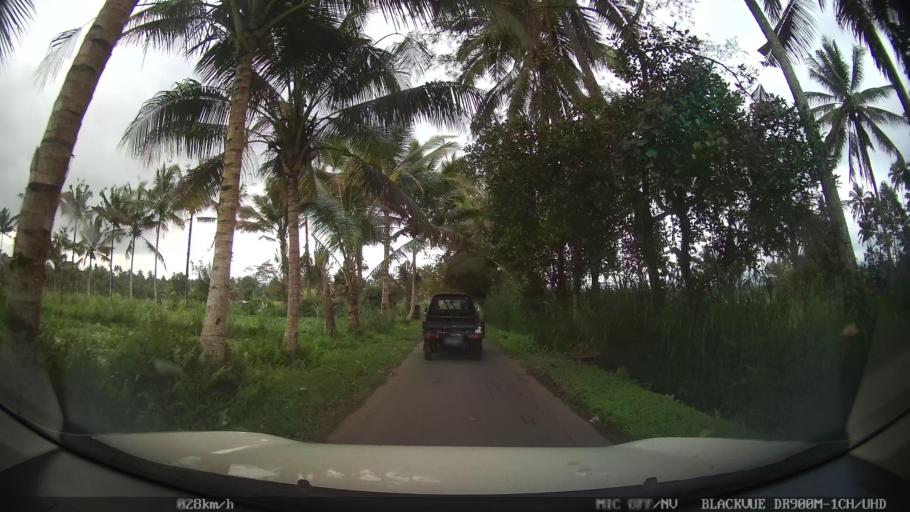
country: ID
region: Bali
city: Banjar Wangsian
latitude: -8.4431
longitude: 115.4255
